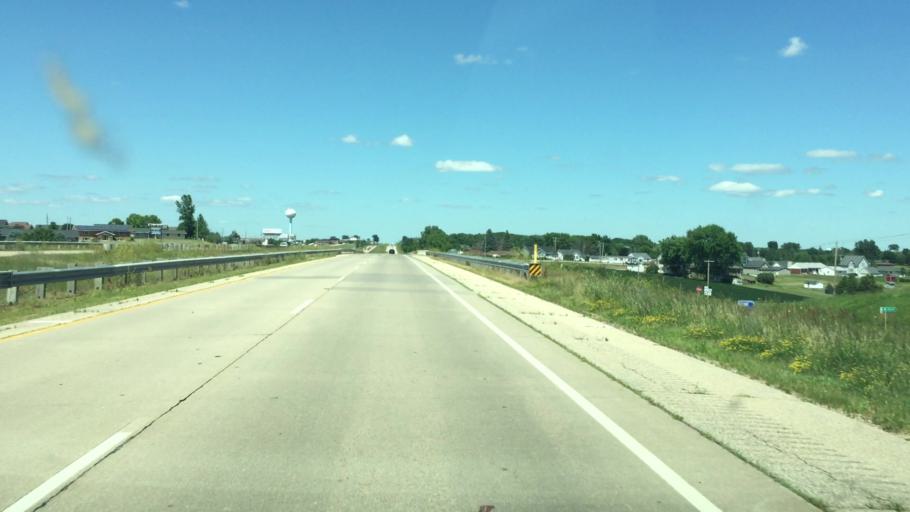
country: US
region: Wisconsin
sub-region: Grant County
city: Dickeyville
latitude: 42.5777
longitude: -90.6087
